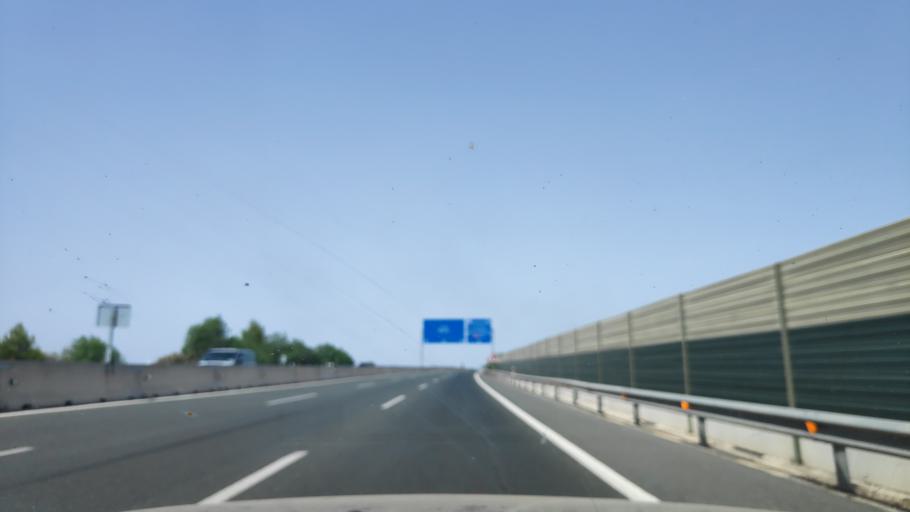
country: ES
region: Murcia
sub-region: Murcia
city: Murcia
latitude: 37.9449
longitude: -1.1481
